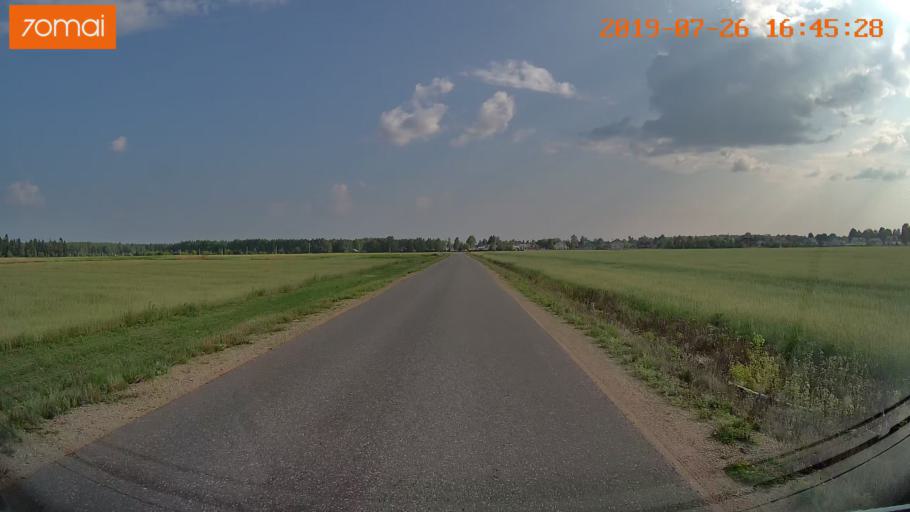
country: RU
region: Ivanovo
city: Bogorodskoye
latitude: 57.0499
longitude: 41.0220
